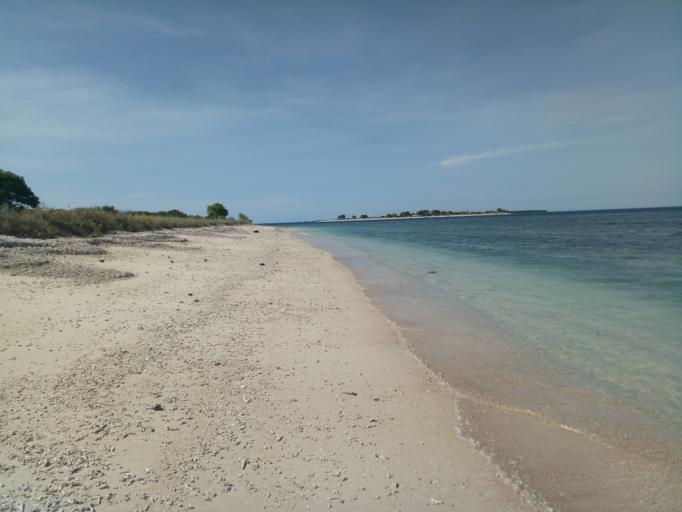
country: ID
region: West Nusa Tenggara
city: Sambelia
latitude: -8.4471
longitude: 116.7325
